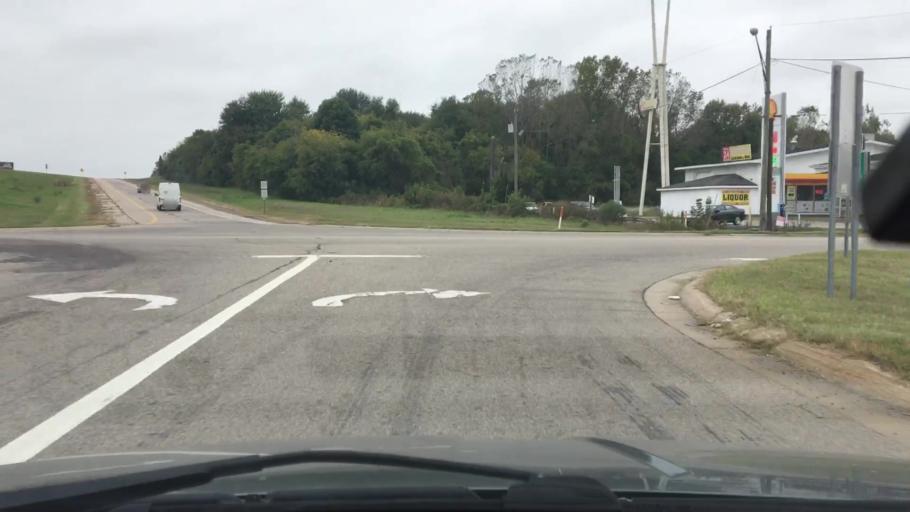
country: US
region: Michigan
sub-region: Berrien County
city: Watervliet
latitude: 42.1789
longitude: -86.2616
